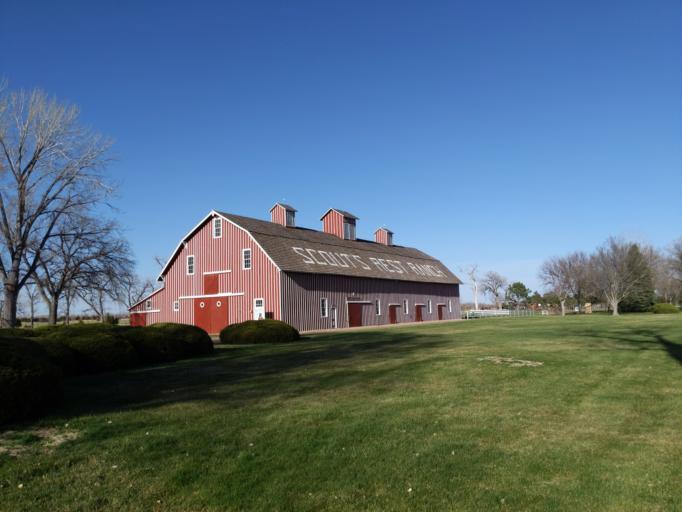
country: US
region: Nebraska
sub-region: Lincoln County
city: North Platte
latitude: 41.1636
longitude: -100.7960
